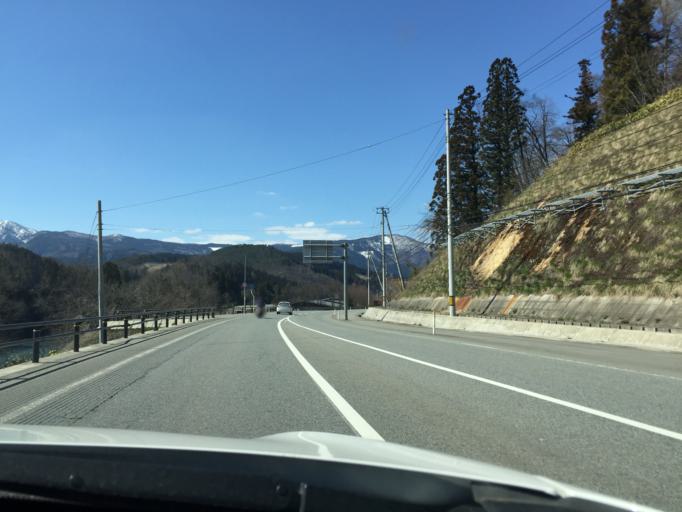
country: JP
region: Yamagata
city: Nagai
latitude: 38.2051
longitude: 140.1024
